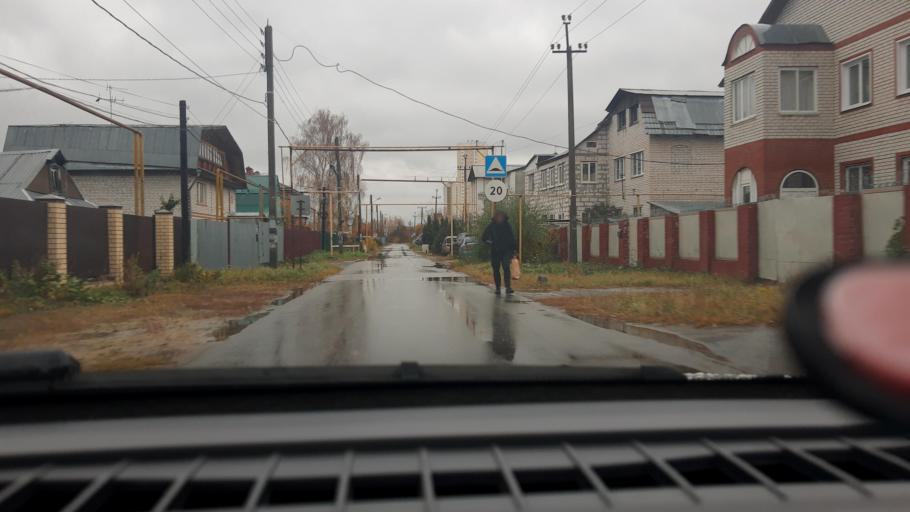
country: RU
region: Nizjnij Novgorod
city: Nizhniy Novgorod
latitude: 56.2975
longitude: 43.9189
